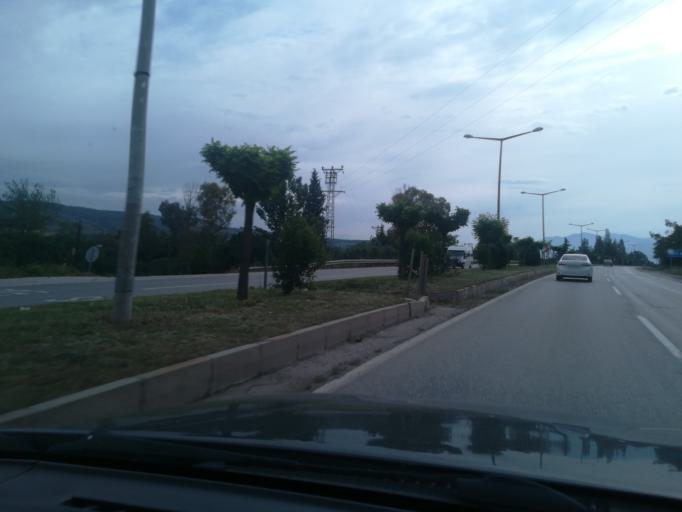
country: TR
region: Osmaniye
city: Toprakkale
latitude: 37.0556
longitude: 36.1647
